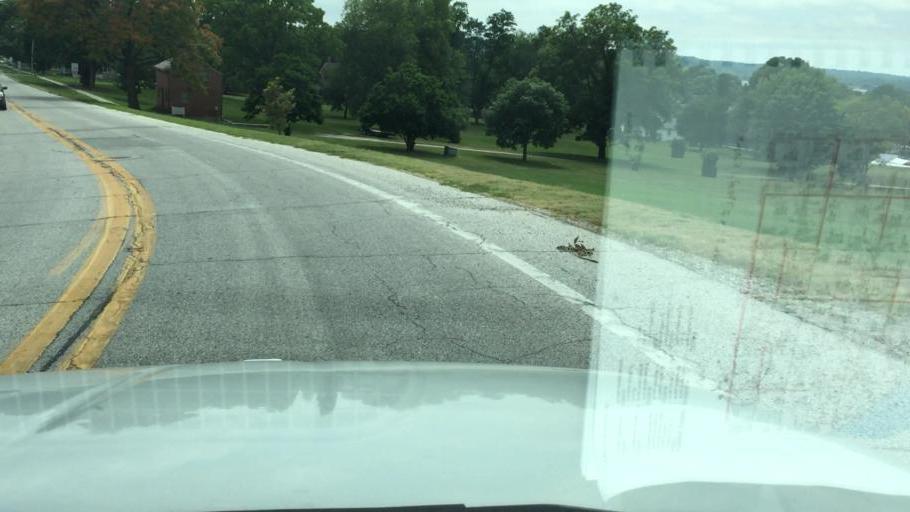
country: US
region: Illinois
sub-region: Hancock County
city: Nauvoo
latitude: 40.5494
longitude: -91.3866
